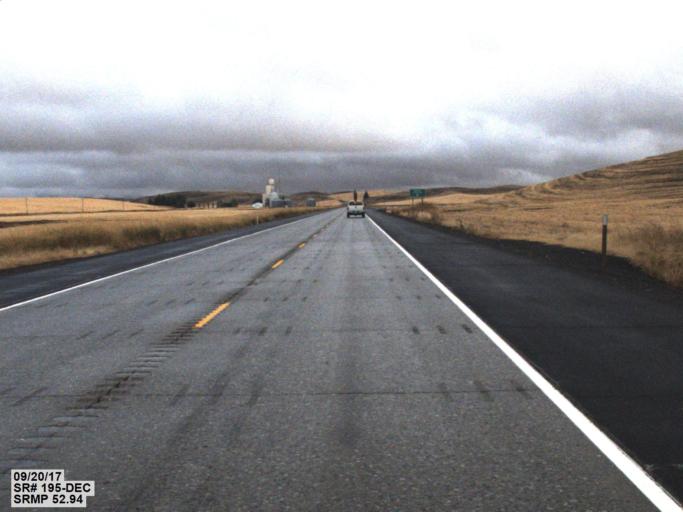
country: US
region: Washington
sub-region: Whitman County
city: Colfax
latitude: 47.0731
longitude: -117.3829
